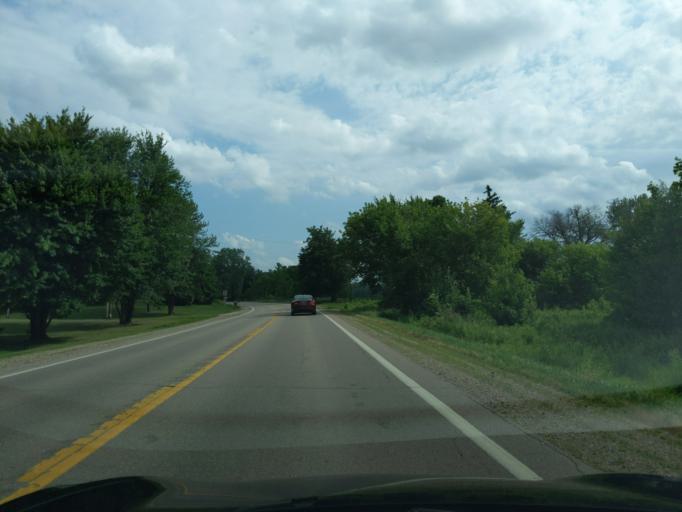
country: US
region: Michigan
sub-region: Eaton County
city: Eaton Rapids
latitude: 42.4643
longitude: -84.6596
